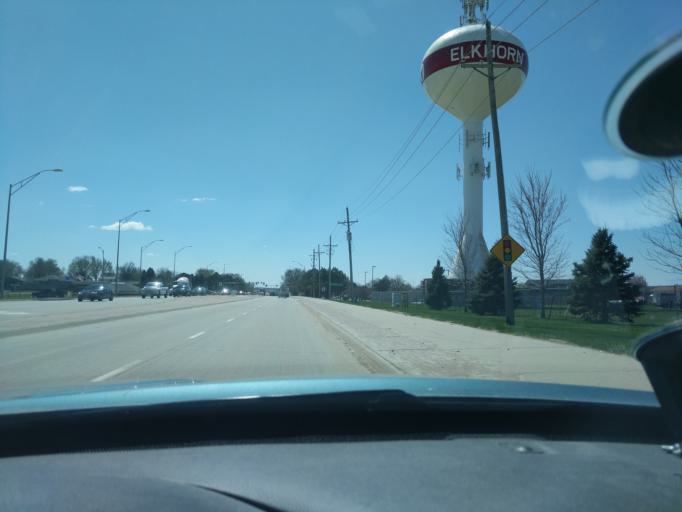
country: US
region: Nebraska
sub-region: Douglas County
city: Elkhorn
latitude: 41.2945
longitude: -96.2345
